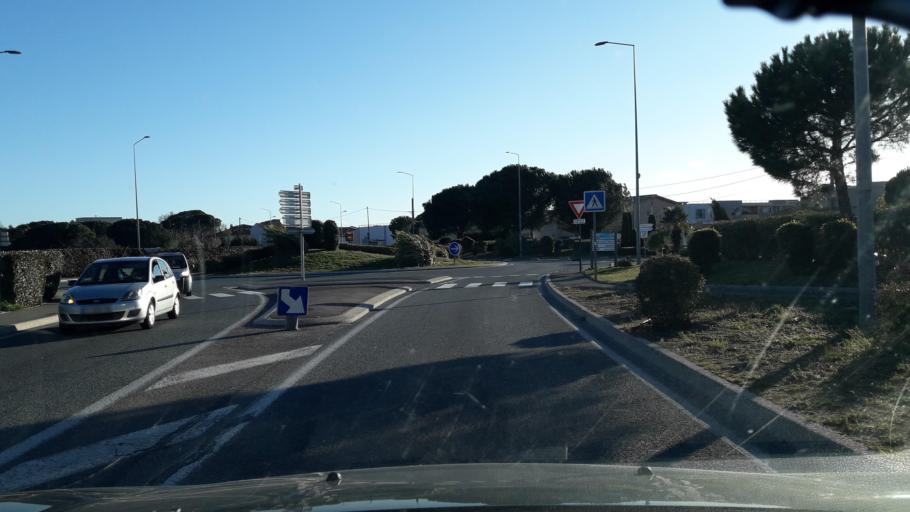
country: FR
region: Provence-Alpes-Cote d'Azur
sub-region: Departement du Var
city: Frejus
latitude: 43.4539
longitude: 6.7268
